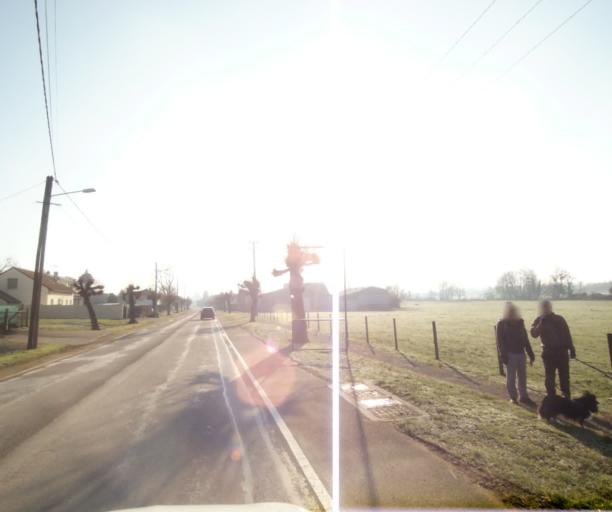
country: FR
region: Champagne-Ardenne
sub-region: Departement de la Haute-Marne
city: Montier-en-Der
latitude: 48.4837
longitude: 4.7625
